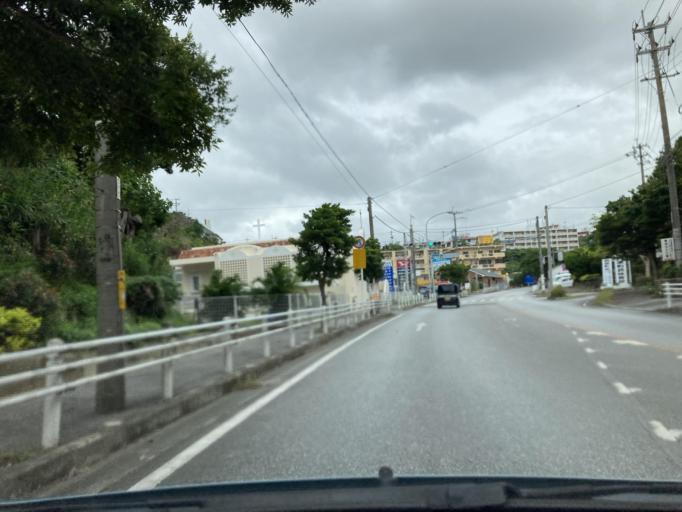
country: JP
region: Okinawa
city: Ginowan
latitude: 26.2339
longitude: 127.7523
